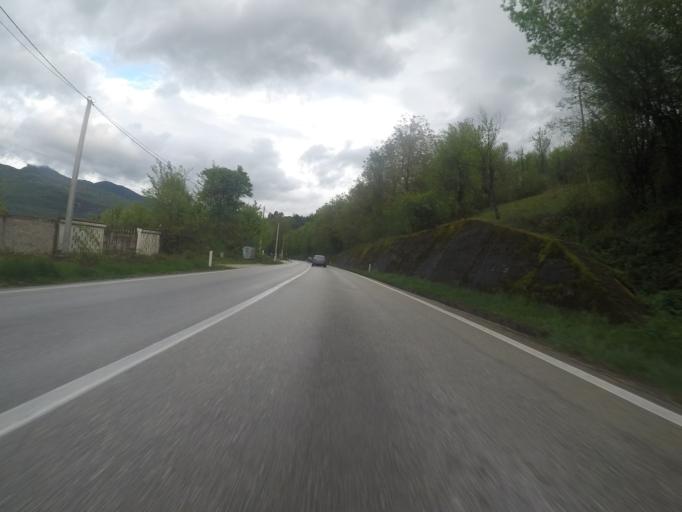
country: BA
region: Federation of Bosnia and Herzegovina
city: Konjic
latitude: 43.6853
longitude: 17.8792
